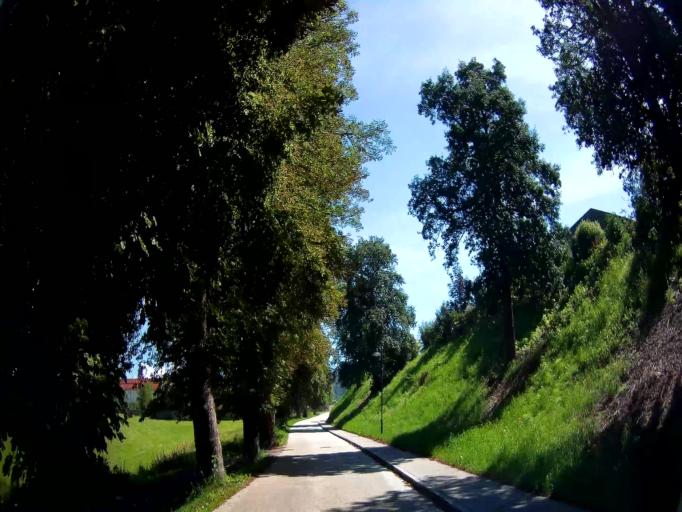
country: AT
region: Carinthia
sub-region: Politischer Bezirk Sankt Veit an der Glan
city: St. Georgen am Laengsee
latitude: 46.7783
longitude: 14.4290
